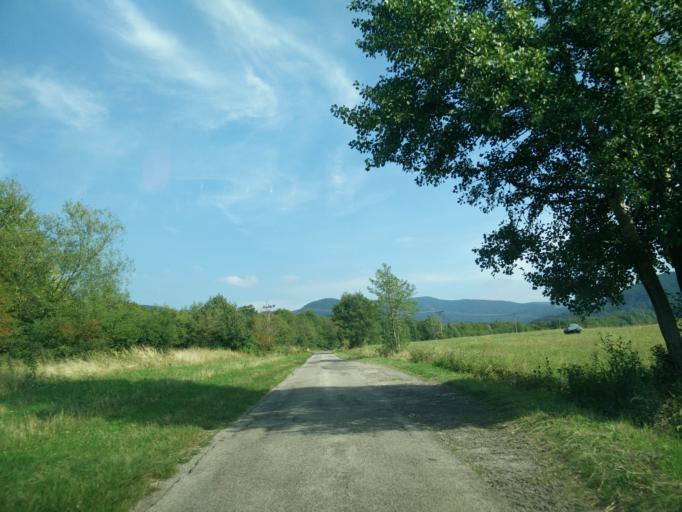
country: SK
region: Nitriansky
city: Novaky
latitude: 48.6867
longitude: 18.6076
